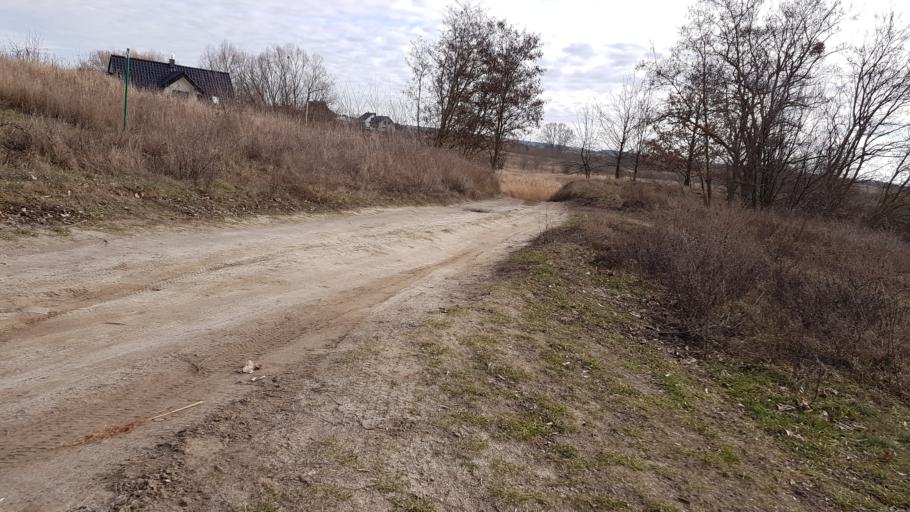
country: PL
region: West Pomeranian Voivodeship
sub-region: Powiat gryfinski
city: Gryfino
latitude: 53.2414
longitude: 14.4935
